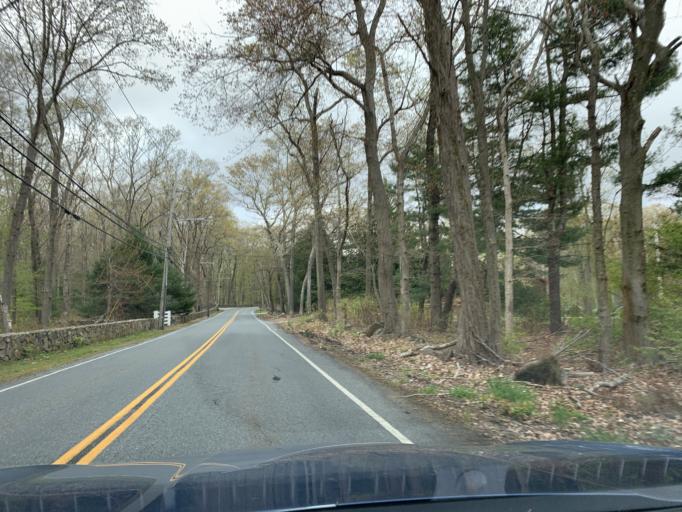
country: US
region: Rhode Island
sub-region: Washington County
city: North Kingstown
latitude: 41.5887
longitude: -71.4693
